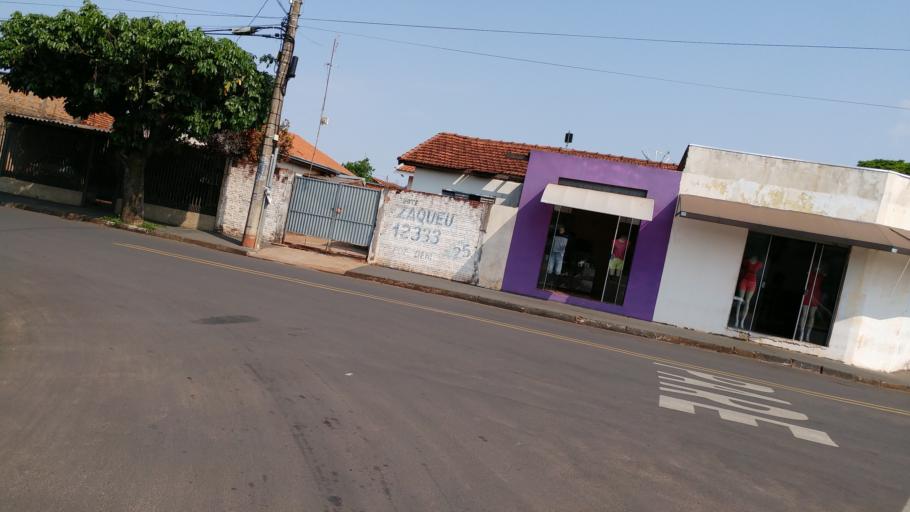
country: BR
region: Sao Paulo
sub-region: Paraguacu Paulista
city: Paraguacu Paulista
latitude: -22.4305
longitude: -50.5837
